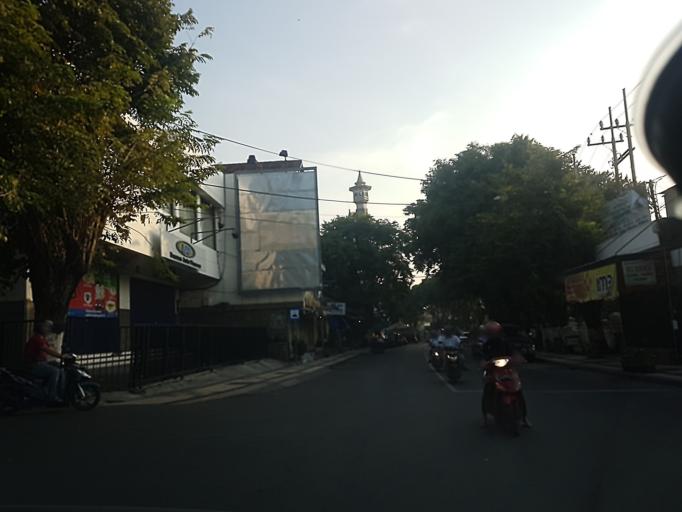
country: ID
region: East Java
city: Gresik
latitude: -7.1583
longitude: 112.6550
